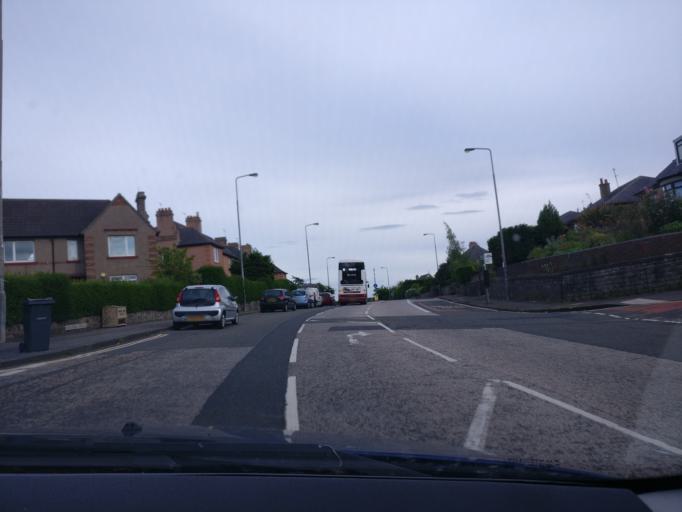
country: GB
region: Scotland
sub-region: West Lothian
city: Seafield
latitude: 55.9510
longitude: -3.1412
